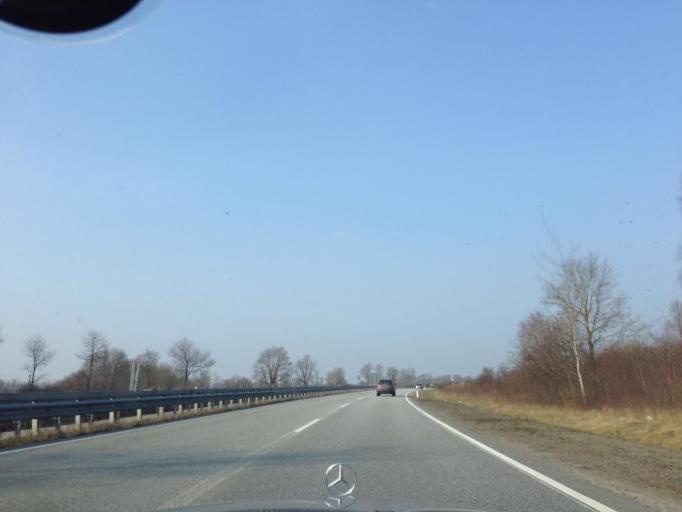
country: DE
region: Schleswig-Holstein
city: Negernbotel
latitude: 53.9744
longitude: 10.2392
